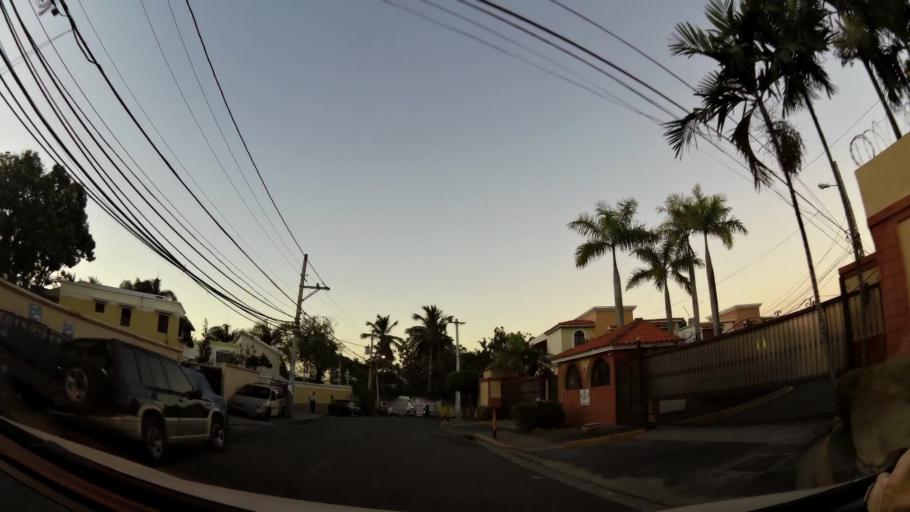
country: DO
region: Nacional
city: La Agustina
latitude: 18.5022
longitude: -69.9520
